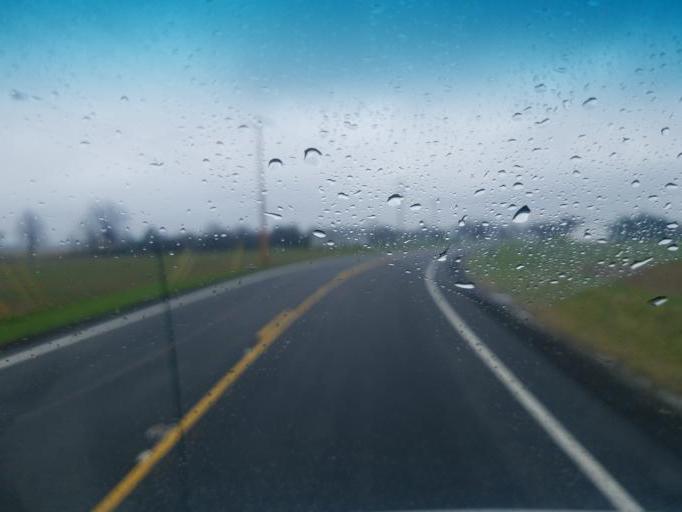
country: US
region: Ohio
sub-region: Huron County
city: Willard
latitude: 40.9652
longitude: -82.8796
